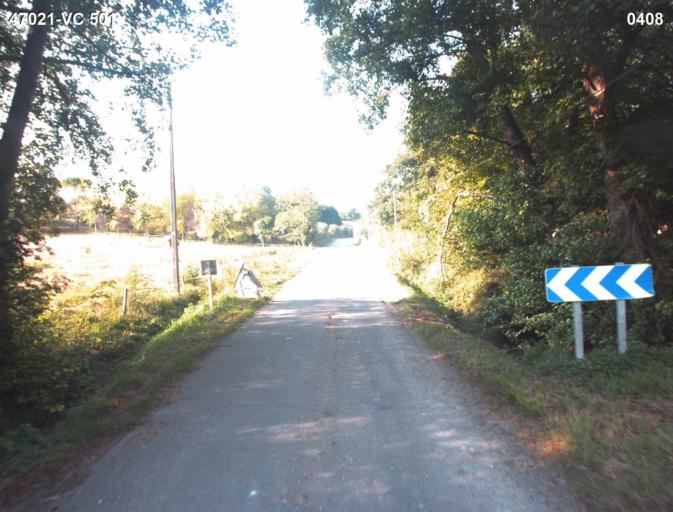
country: FR
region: Aquitaine
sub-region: Departement du Lot-et-Garonne
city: Barbaste
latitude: 44.1813
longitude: 0.2550
